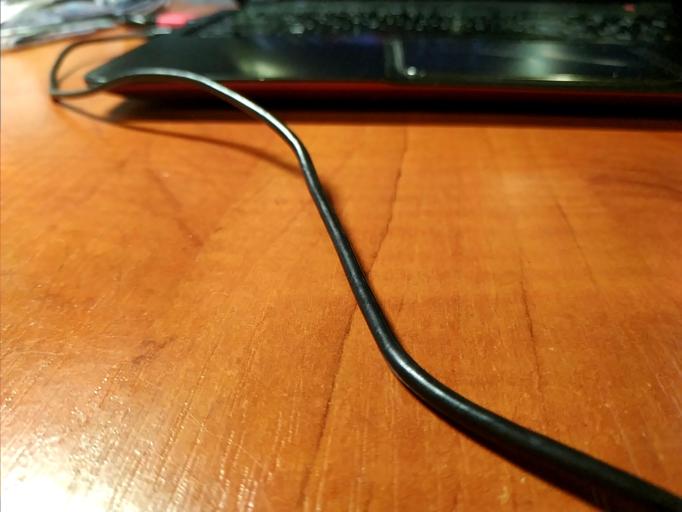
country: RU
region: Tverskaya
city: Zubtsov
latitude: 56.3125
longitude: 34.6802
